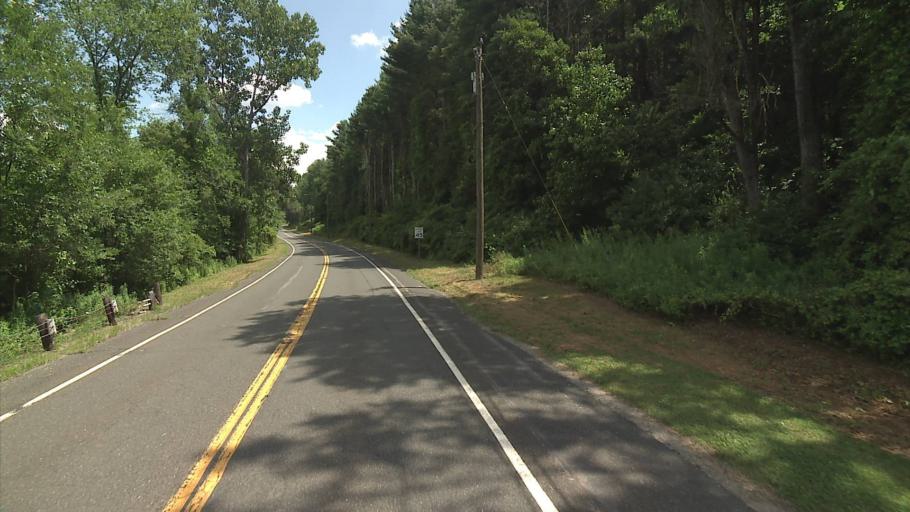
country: US
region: Connecticut
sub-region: Litchfield County
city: Canaan
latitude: 41.9479
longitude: -73.3295
